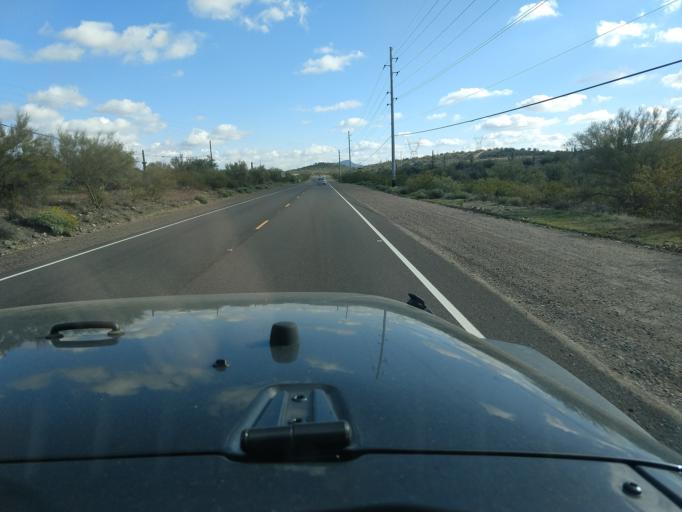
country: US
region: Arizona
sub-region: Maricopa County
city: New River
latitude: 33.9193
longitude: -112.1037
